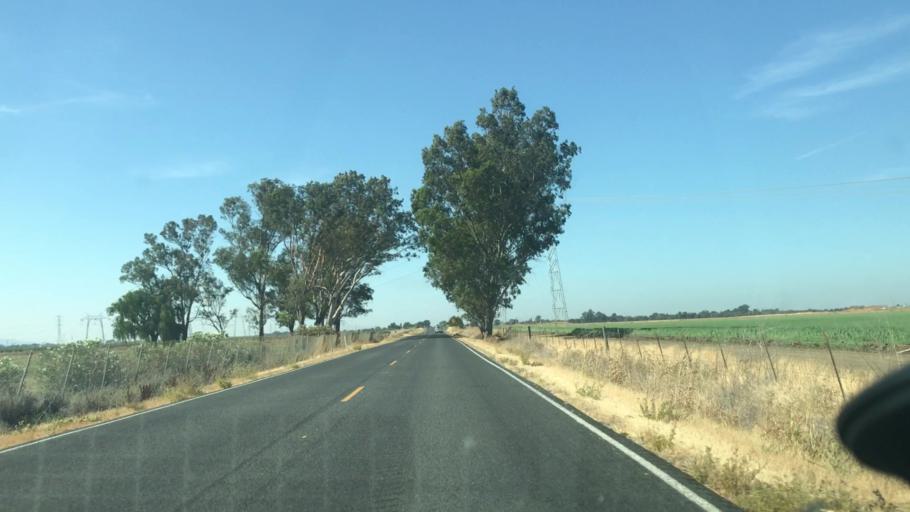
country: US
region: California
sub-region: Solano County
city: Vacaville
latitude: 38.3265
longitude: -121.9154
